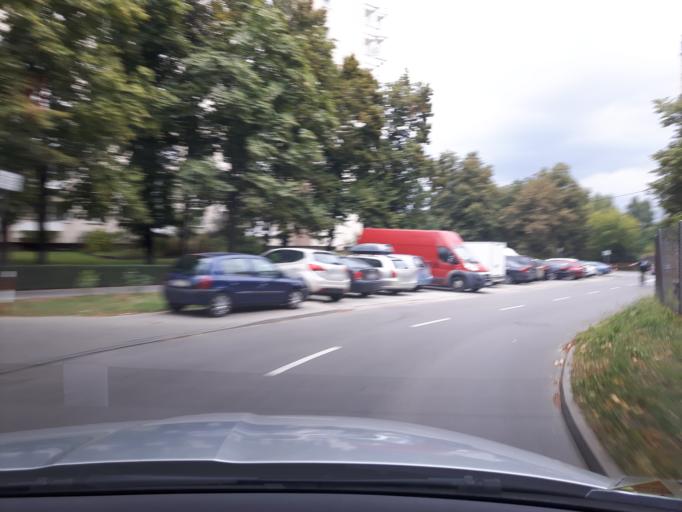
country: PL
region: Masovian Voivodeship
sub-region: Warszawa
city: Mokotow
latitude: 52.1698
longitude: 21.0215
